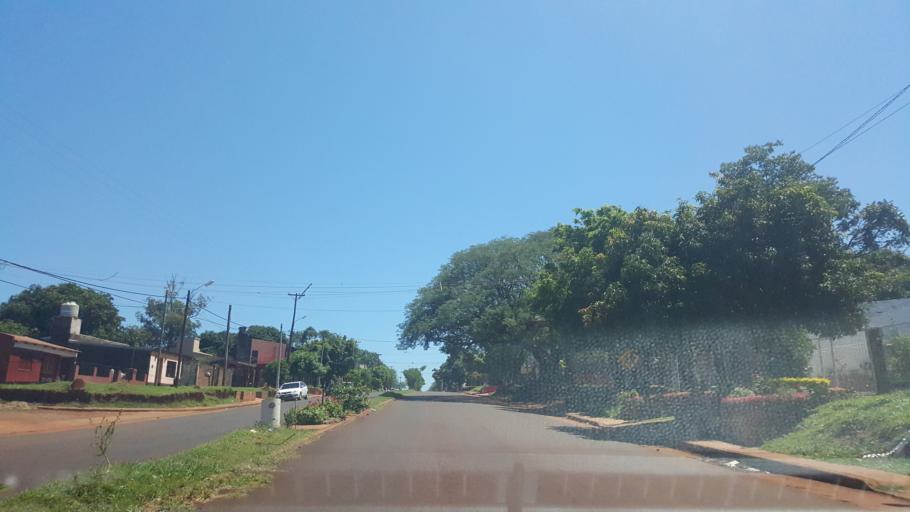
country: AR
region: Misiones
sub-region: Departamento de Capital
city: Posadas
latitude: -27.3897
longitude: -55.9310
